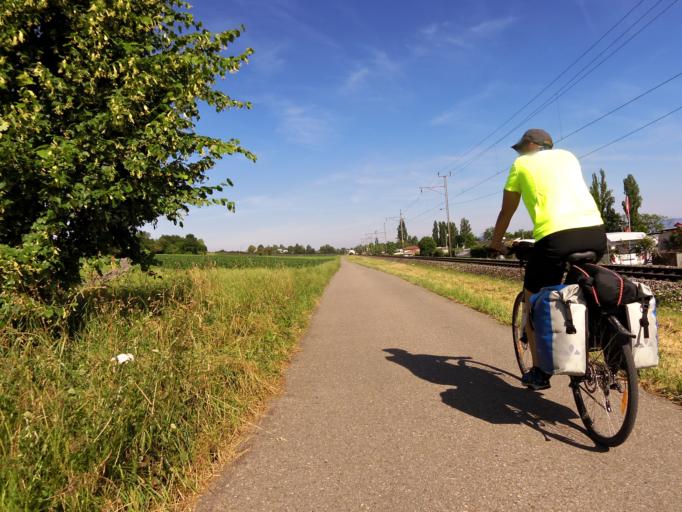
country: CH
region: Thurgau
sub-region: Kreuzlingen District
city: Altnau
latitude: 47.6235
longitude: 9.2607
